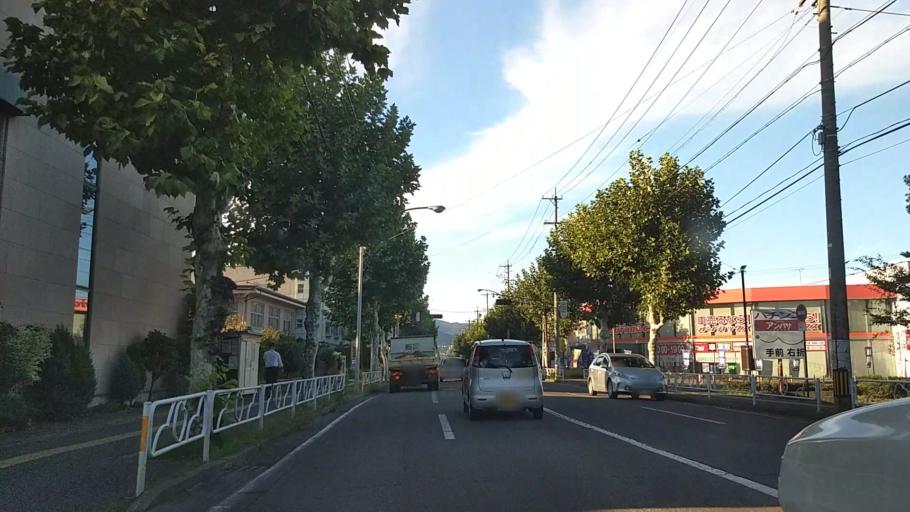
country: JP
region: Nagano
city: Nagano-shi
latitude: 36.6352
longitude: 138.1999
